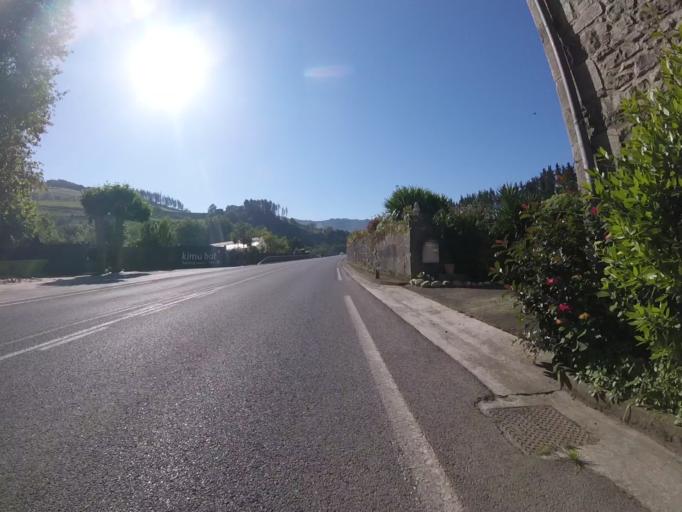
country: ES
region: Basque Country
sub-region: Provincia de Guipuzcoa
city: Azpeitia
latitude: 43.1699
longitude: -2.2529
